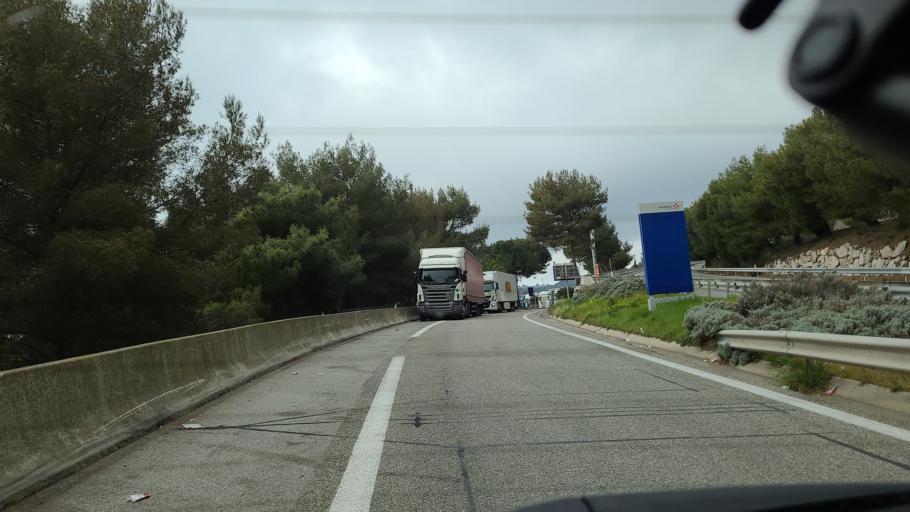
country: FR
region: Provence-Alpes-Cote d'Azur
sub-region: Departement des Alpes-Maritimes
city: Beausoleil
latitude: 43.7544
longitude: 7.4211
